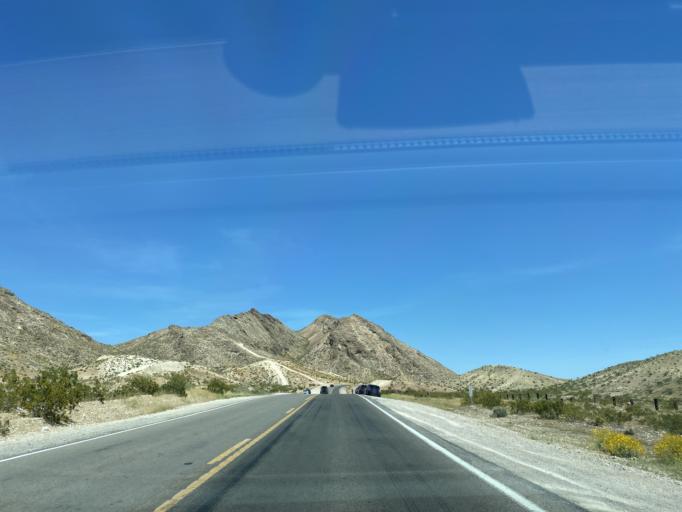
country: US
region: Nevada
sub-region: Clark County
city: Nellis Air Force Base
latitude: 36.2017
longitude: -114.9913
